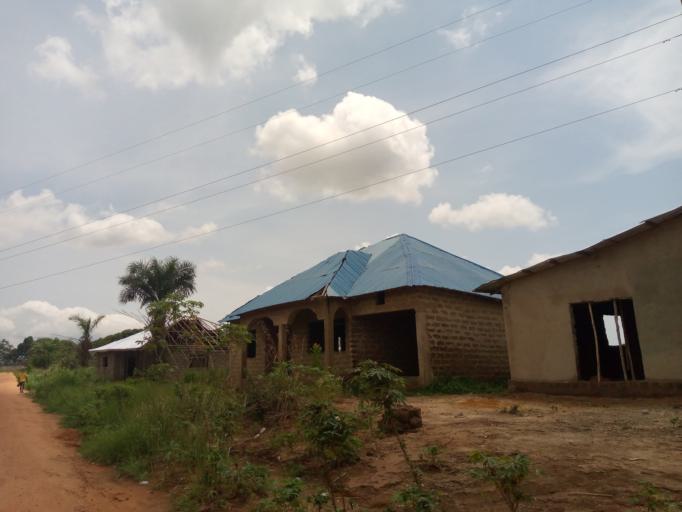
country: SL
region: Western Area
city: Waterloo
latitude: 8.3581
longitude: -12.9675
